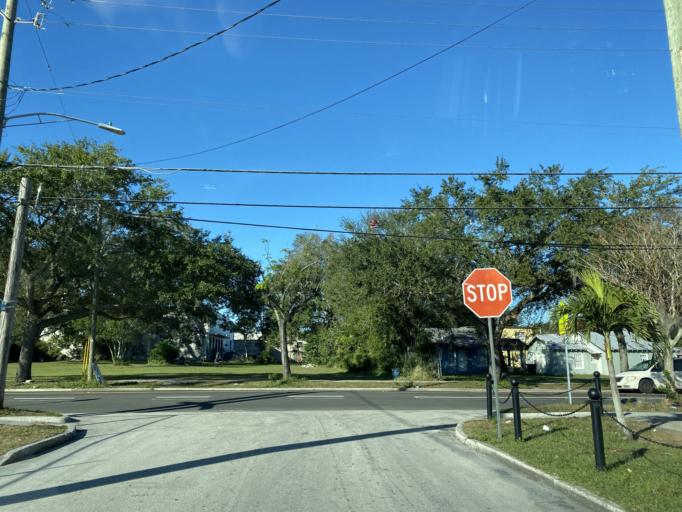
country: US
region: Florida
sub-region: Orange County
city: Orlando
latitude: 28.5434
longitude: -81.3888
